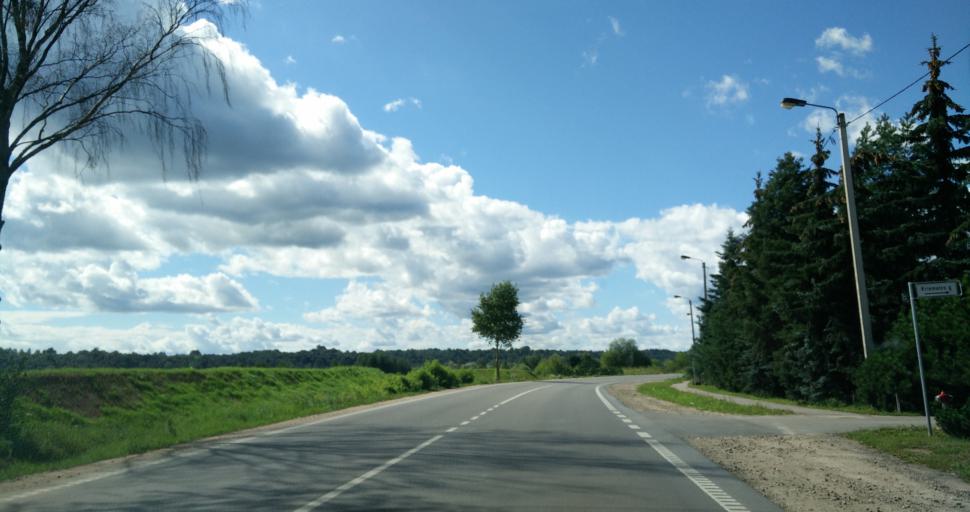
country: LT
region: Kauno apskritis
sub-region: Kauno rajonas
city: Akademija (Kaunas)
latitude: 54.9208
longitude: 23.8040
